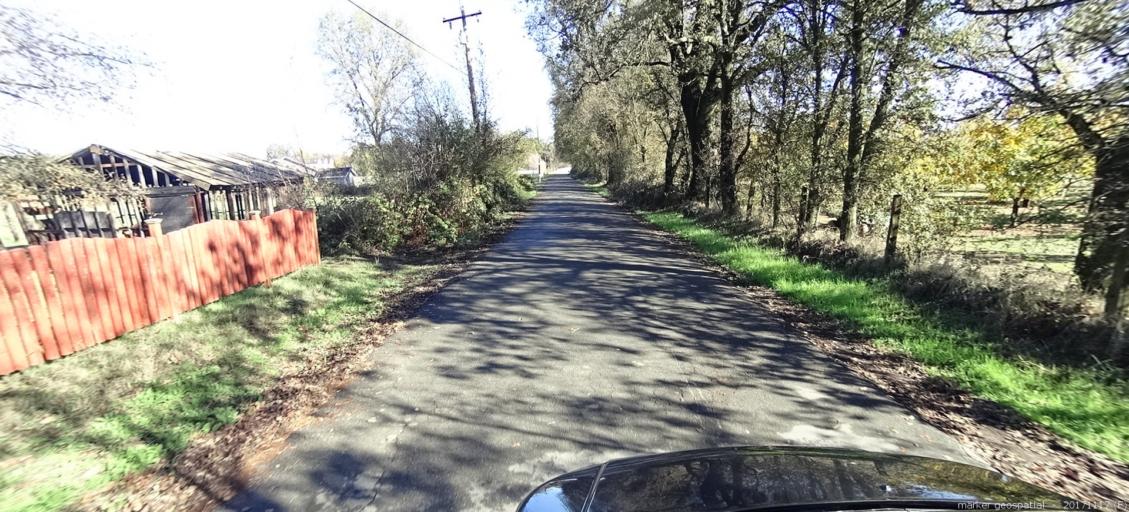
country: US
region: California
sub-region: Shasta County
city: Cottonwood
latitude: 40.4208
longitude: -122.2172
